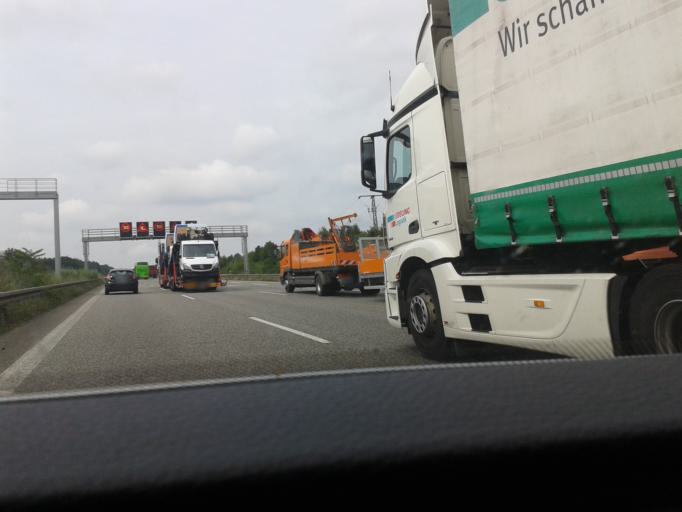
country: DE
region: Saxony-Anhalt
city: Wefensleben
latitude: 52.2077
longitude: 11.1269
